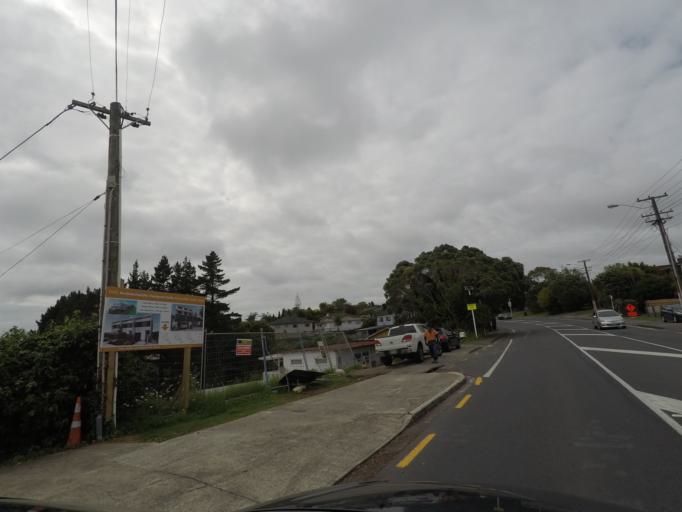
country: NZ
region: Auckland
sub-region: Auckland
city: Rosebank
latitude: -36.8402
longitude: 174.6004
